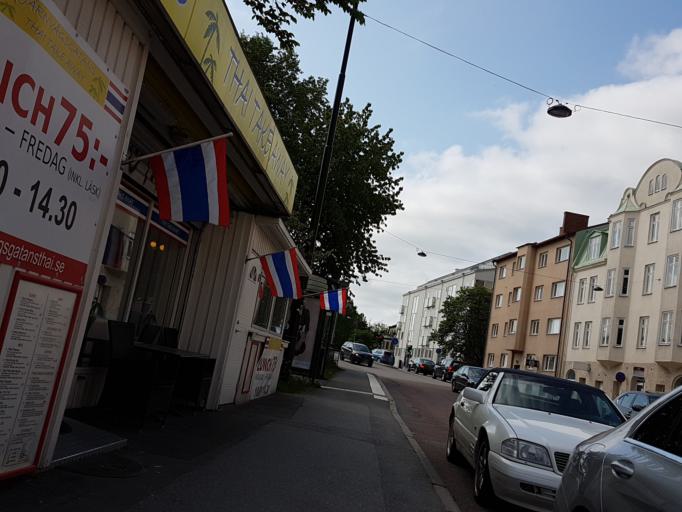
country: SE
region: Stockholm
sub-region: Sundbybergs Kommun
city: Sundbyberg
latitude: 59.3653
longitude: 17.9577
